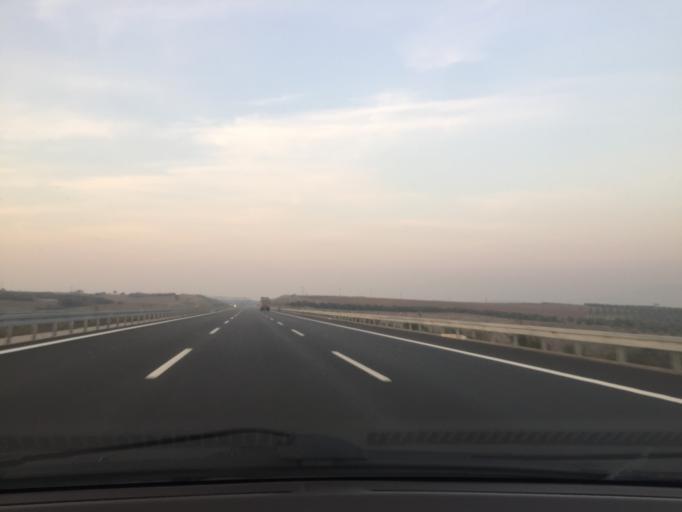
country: TR
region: Bursa
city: Karacabey
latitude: 40.2666
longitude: 28.4923
